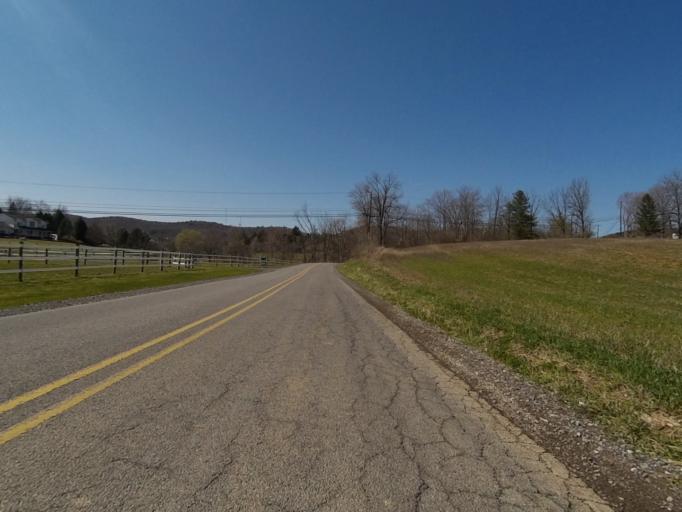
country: US
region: Pennsylvania
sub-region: Centre County
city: Stormstown
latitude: 40.7714
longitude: -78.0399
